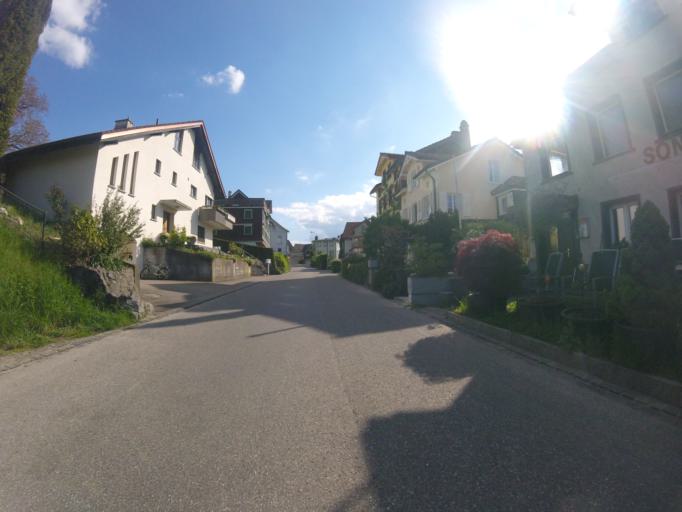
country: CH
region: Saint Gallen
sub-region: Wahlkreis Toggenburg
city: Mogelsberg
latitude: 47.3637
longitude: 9.1368
